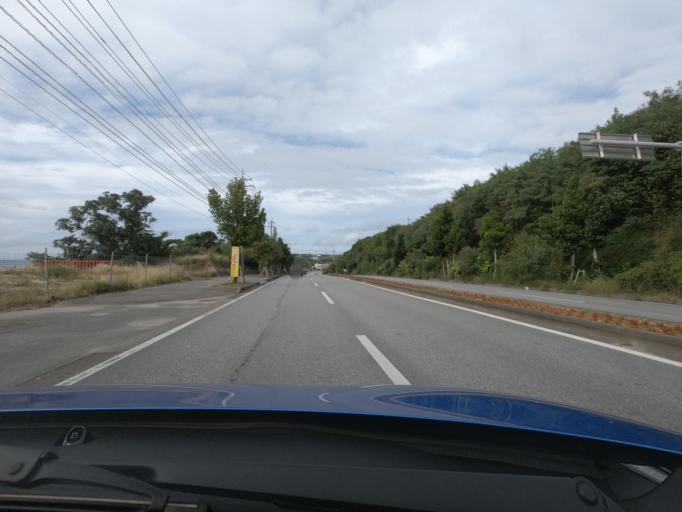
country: JP
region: Okinawa
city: Nago
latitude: 26.6669
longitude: 127.8904
